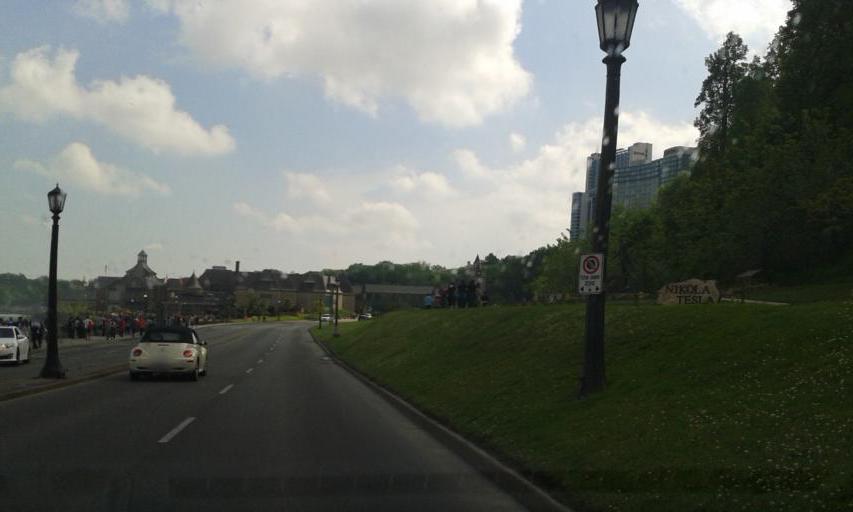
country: CA
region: Ontario
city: Niagara Falls
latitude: 43.0821
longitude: -79.0782
